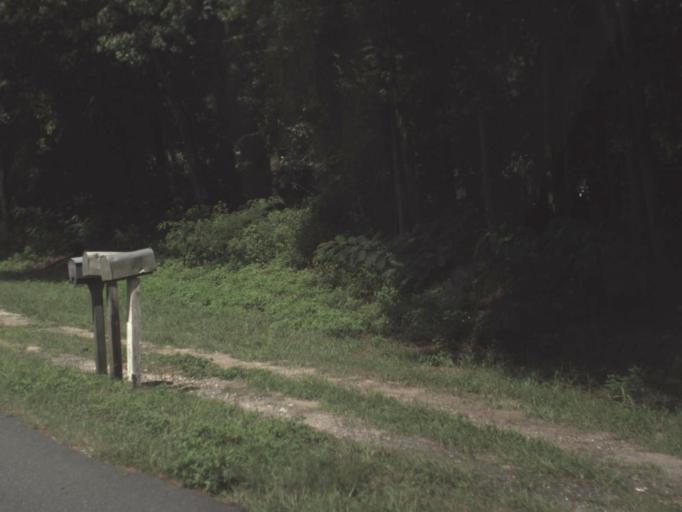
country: US
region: Florida
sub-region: Alachua County
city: Alachua
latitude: 29.8054
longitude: -82.4741
